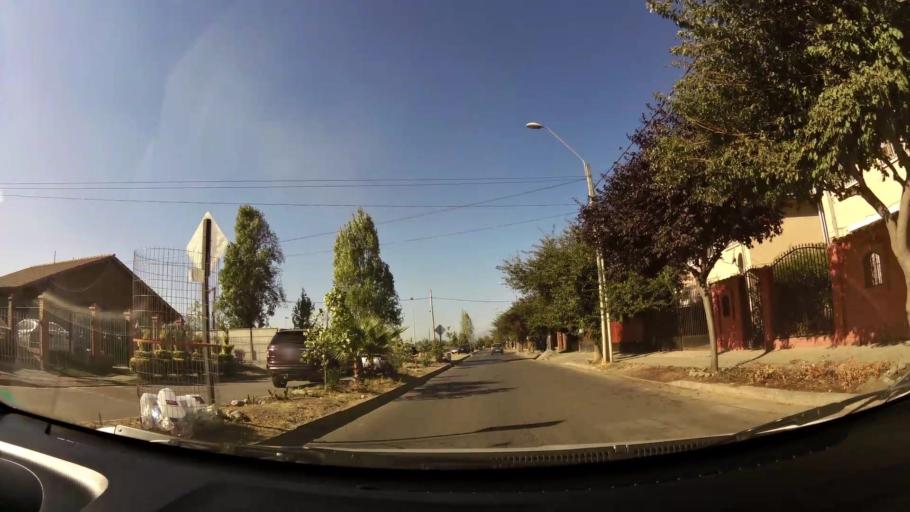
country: CL
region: O'Higgins
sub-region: Provincia de Cachapoal
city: Rancagua
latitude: -34.1805
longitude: -70.7601
